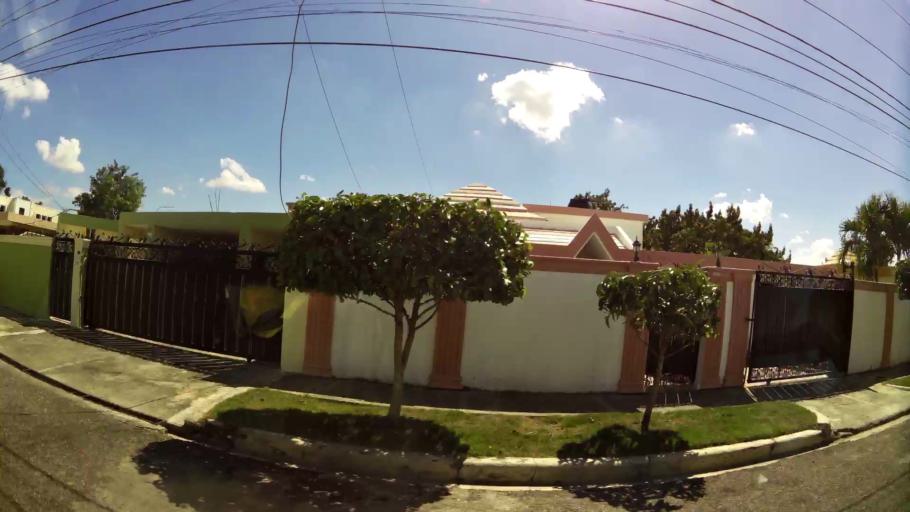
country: DO
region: Santiago
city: Santiago de los Caballeros
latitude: 19.4441
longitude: -70.6919
